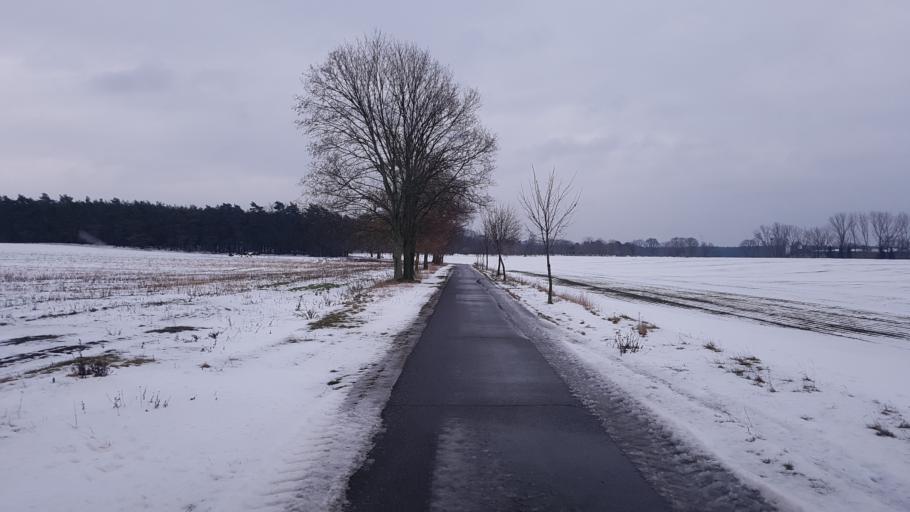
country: DE
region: Brandenburg
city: Bronkow
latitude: 51.6540
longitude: 13.9279
